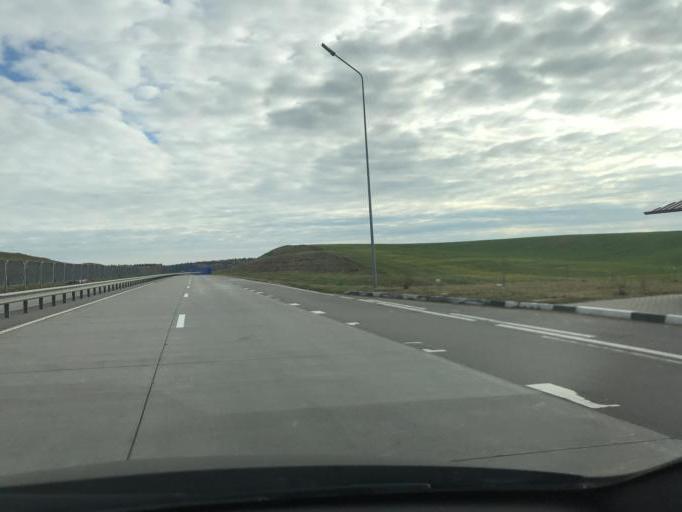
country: BY
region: Minsk
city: Pyatryshki
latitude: 54.0713
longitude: 27.2749
